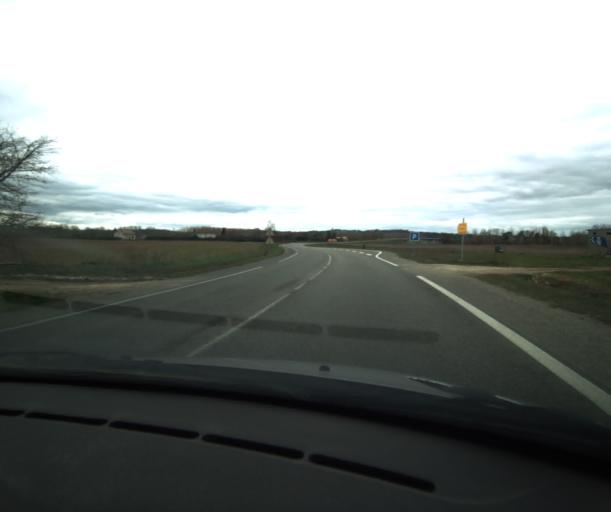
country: FR
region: Midi-Pyrenees
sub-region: Departement du Tarn-et-Garonne
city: Moissac
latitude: 44.0857
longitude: 1.1169
